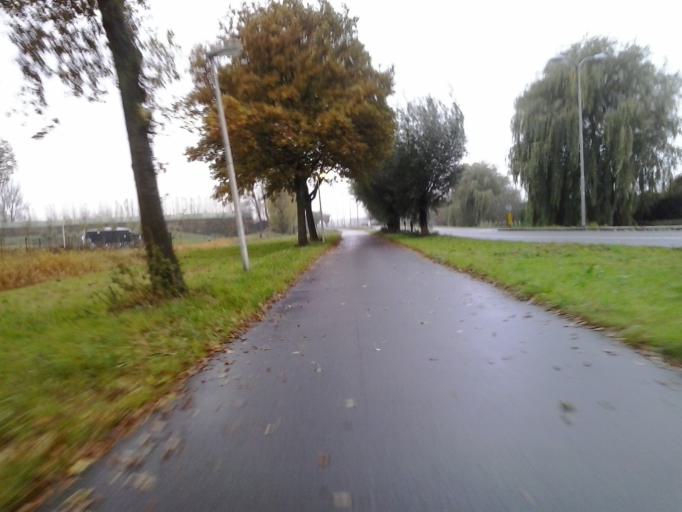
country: NL
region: South Holland
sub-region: Gemeente Zoetermeer
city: Zoetermeer
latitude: 52.0309
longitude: 4.5040
